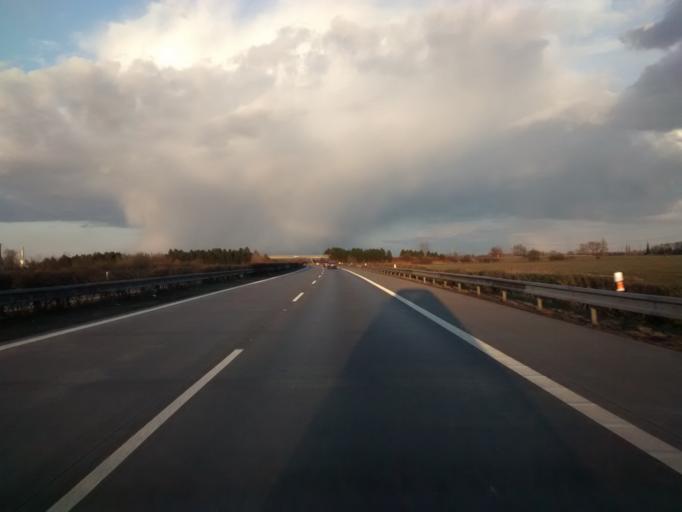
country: CZ
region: Central Bohemia
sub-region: Okres Nymburk
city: Sadska
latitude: 50.1161
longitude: 14.9651
